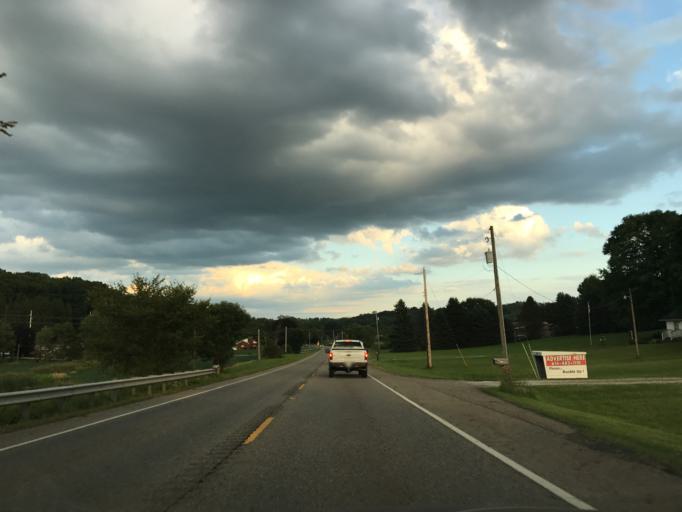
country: US
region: Ohio
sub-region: Carroll County
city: Malvern
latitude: 40.7648
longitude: -81.2078
